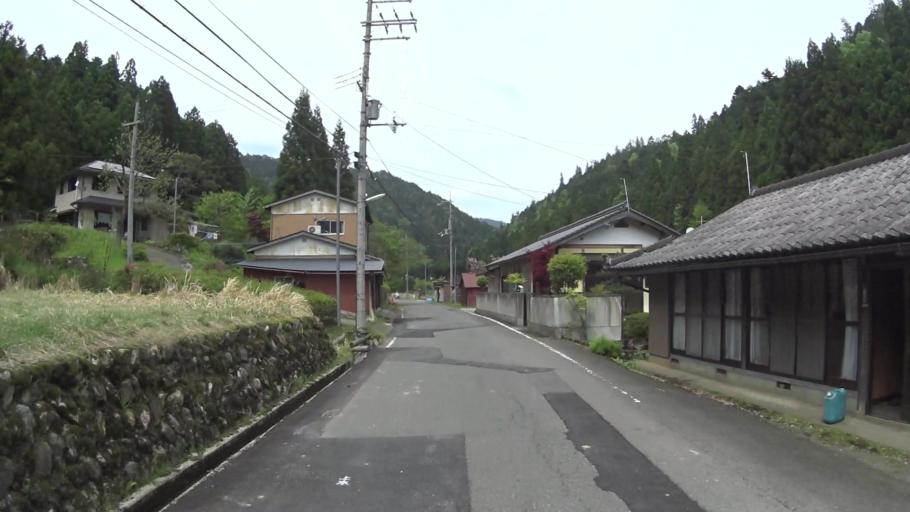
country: JP
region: Kyoto
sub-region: Kyoto-shi
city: Kamigyo-ku
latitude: 35.2152
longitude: 135.7011
